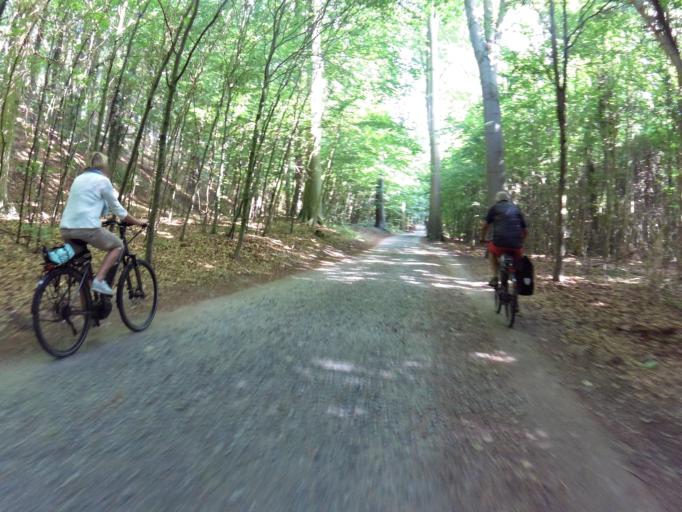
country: DE
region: Mecklenburg-Vorpommern
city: Koserow
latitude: 54.0533
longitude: 14.0097
